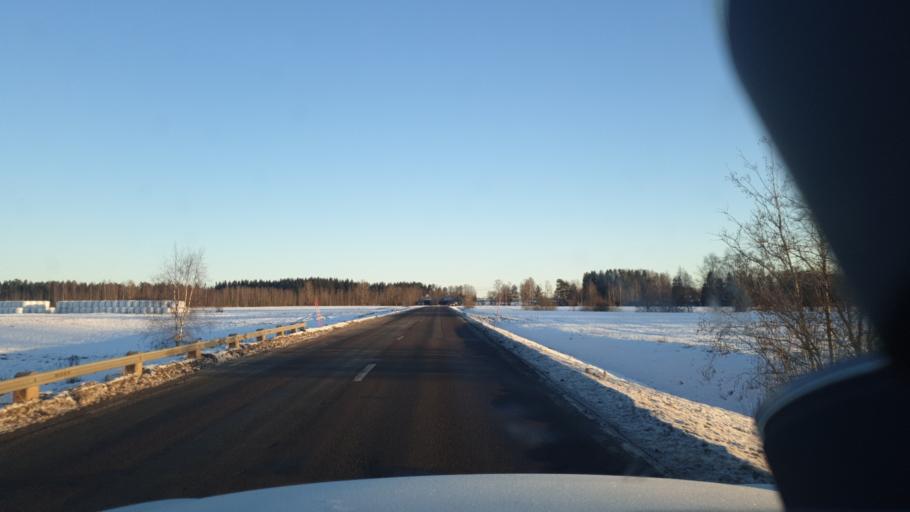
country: SE
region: Vaermland
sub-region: Sunne Kommun
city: Sunne
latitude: 59.7258
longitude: 13.1202
